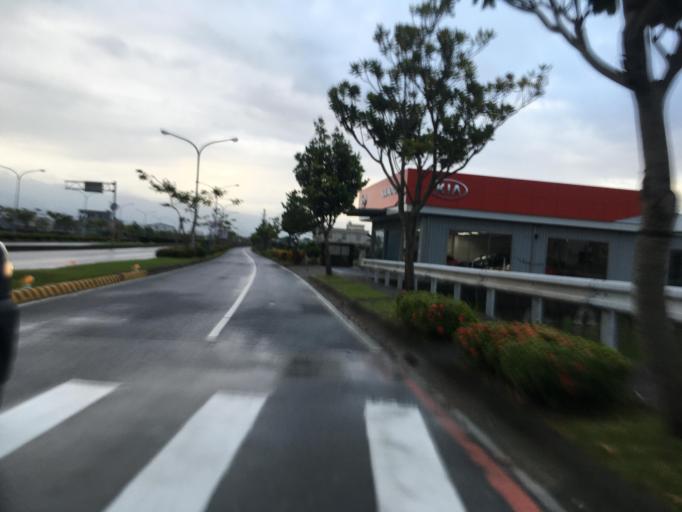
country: TW
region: Taiwan
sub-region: Yilan
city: Yilan
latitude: 24.7258
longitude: 121.7724
